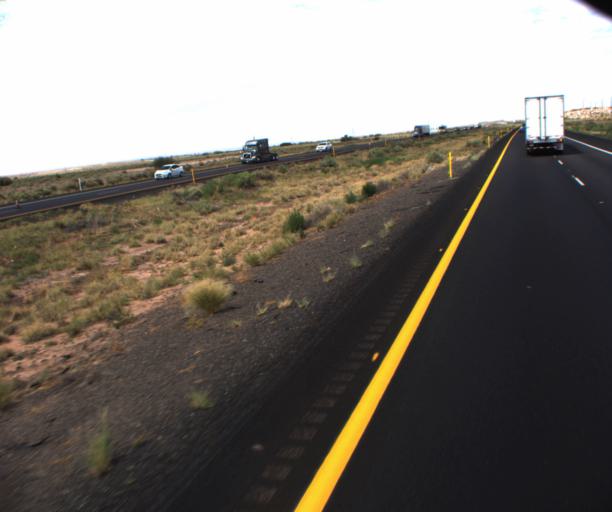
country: US
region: Arizona
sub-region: Navajo County
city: Holbrook
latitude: 34.9938
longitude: -109.9395
